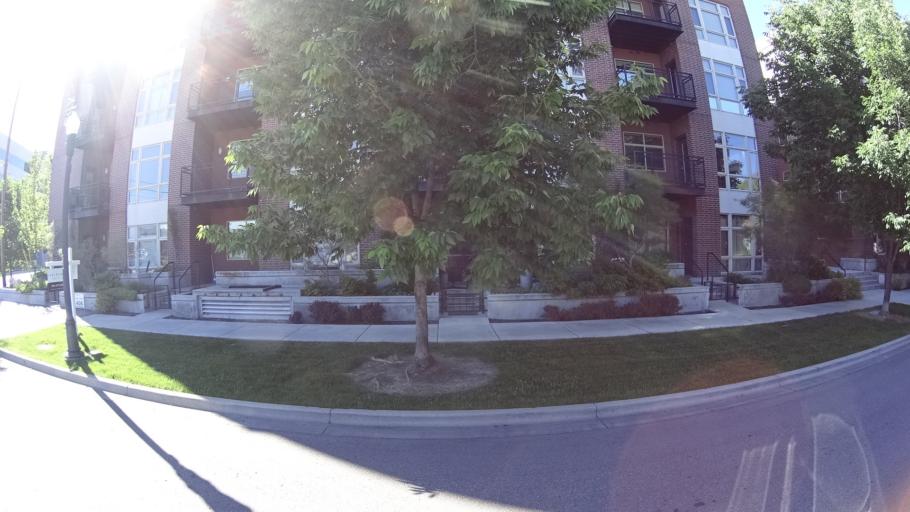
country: US
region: Idaho
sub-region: Ada County
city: Boise
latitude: 43.6160
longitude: -116.2121
